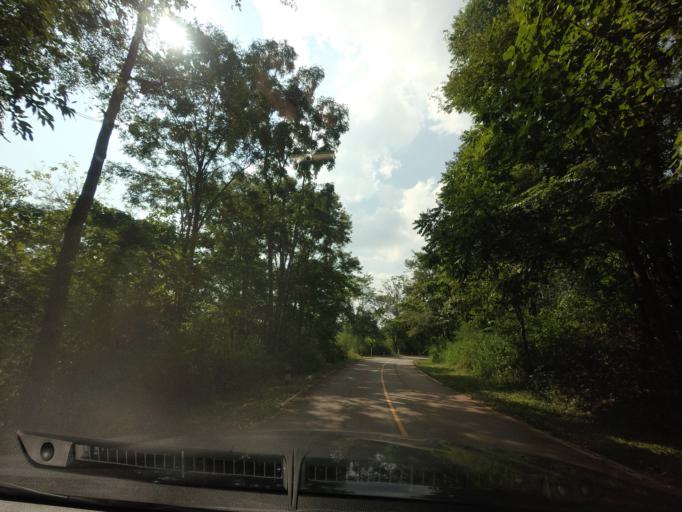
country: TH
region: Uttaradit
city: Ban Khok
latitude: 18.1799
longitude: 101.0681
